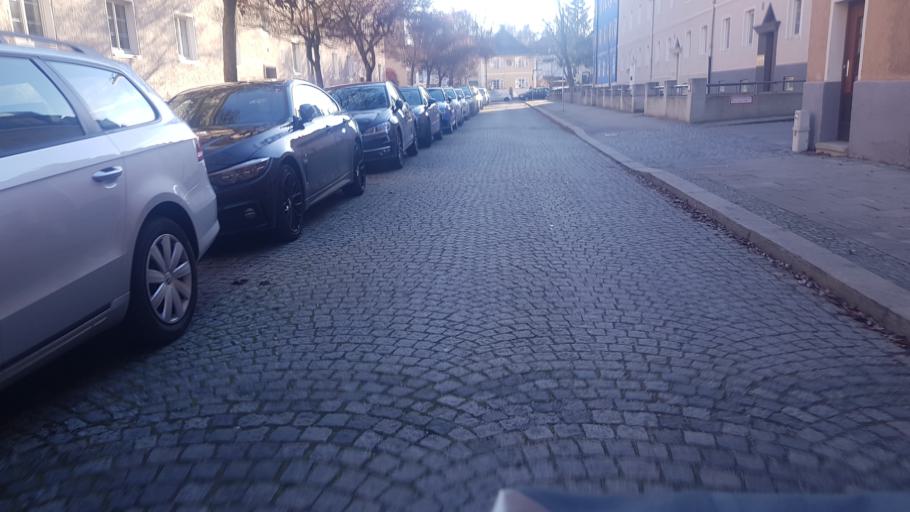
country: DE
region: Bavaria
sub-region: Upper Bavaria
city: Pasing
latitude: 48.1527
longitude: 11.5104
